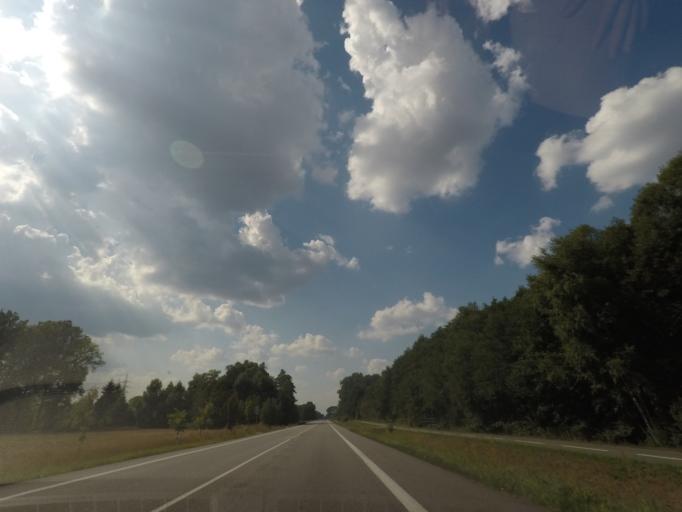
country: CZ
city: Tyniste nad Orlici
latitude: 50.1595
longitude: 16.0603
